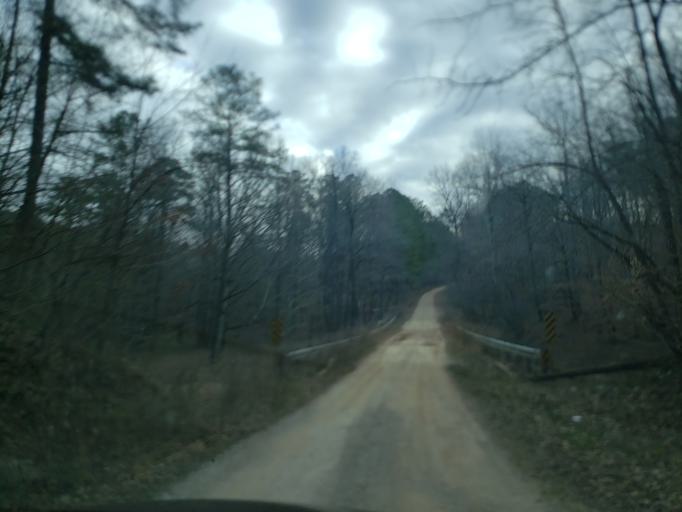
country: US
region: Alabama
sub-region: Cleburne County
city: Heflin
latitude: 33.7133
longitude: -85.6187
